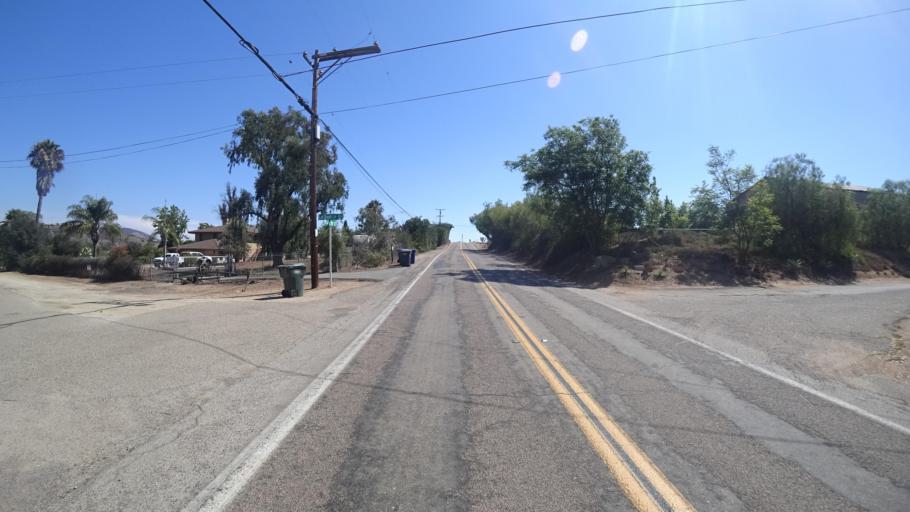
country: US
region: California
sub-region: San Diego County
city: Hidden Meadows
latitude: 33.2731
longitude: -117.1122
